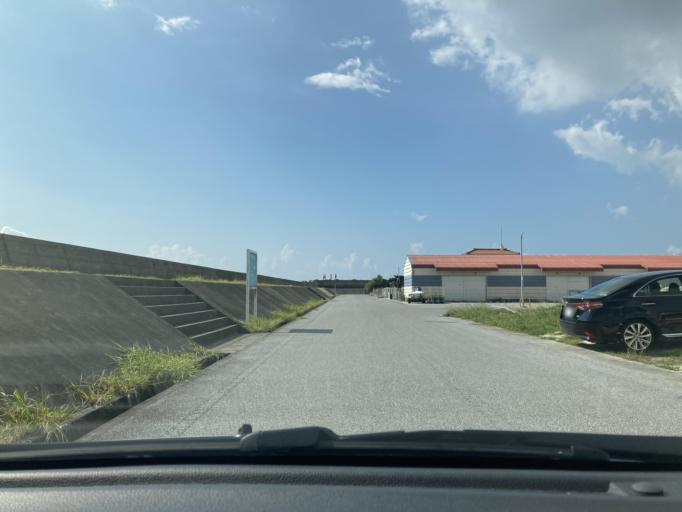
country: JP
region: Okinawa
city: Itoman
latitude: 26.1306
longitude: 127.7767
